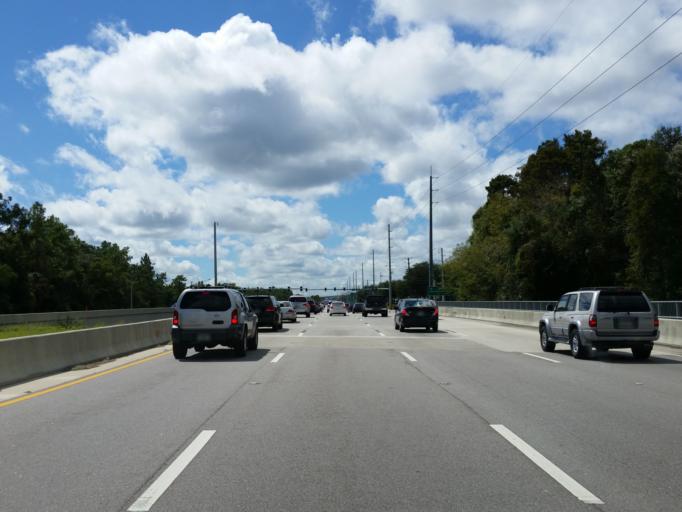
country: US
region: Florida
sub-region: Hillsborough County
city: Pebble Creek
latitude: 28.1349
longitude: -82.3614
